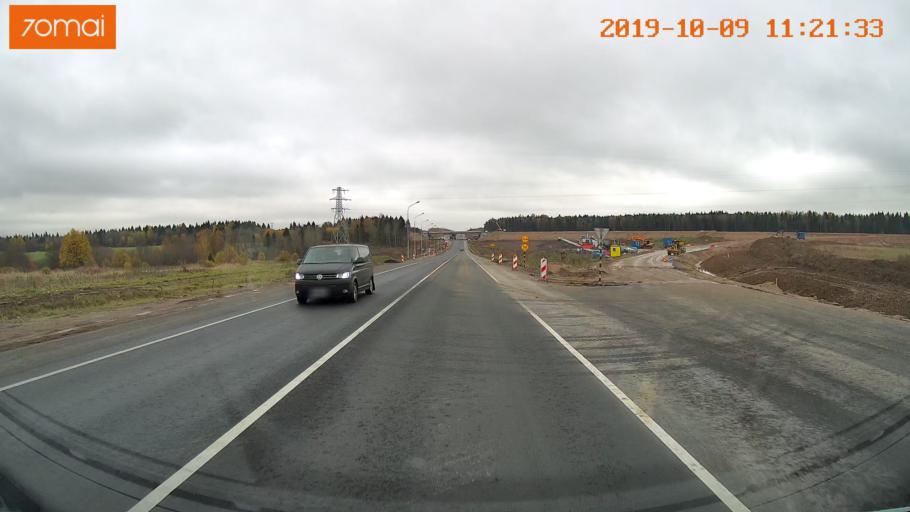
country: RU
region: Vologda
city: Vologda
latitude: 59.1387
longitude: 39.9503
